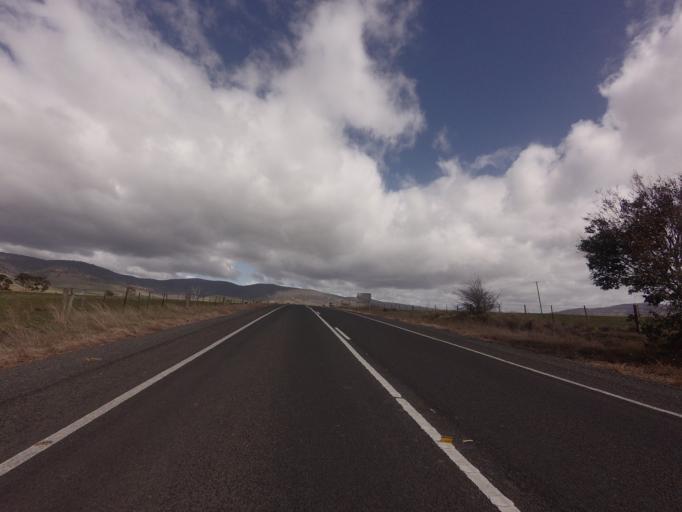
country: AU
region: Tasmania
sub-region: Northern Midlands
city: Evandale
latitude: -41.8056
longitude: 147.6812
